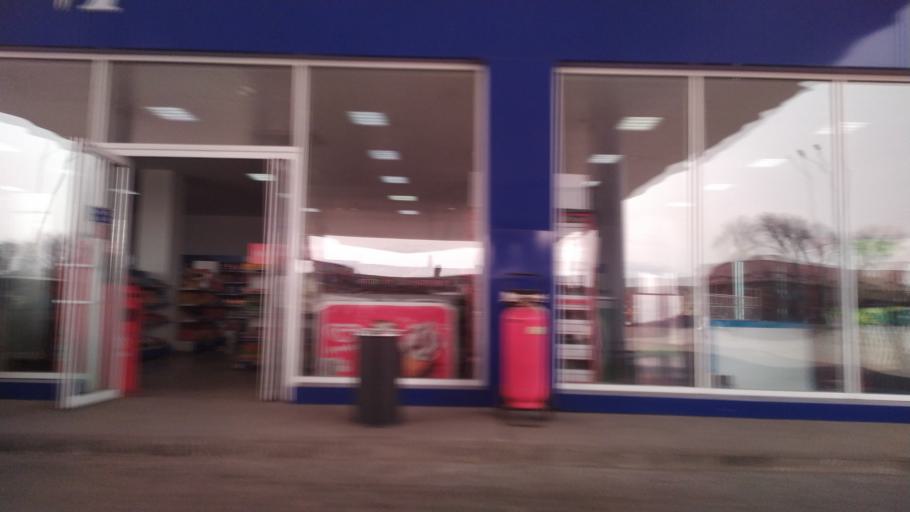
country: KZ
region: Almaty Oblysy
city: Burunday
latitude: 43.2216
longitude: 76.5411
